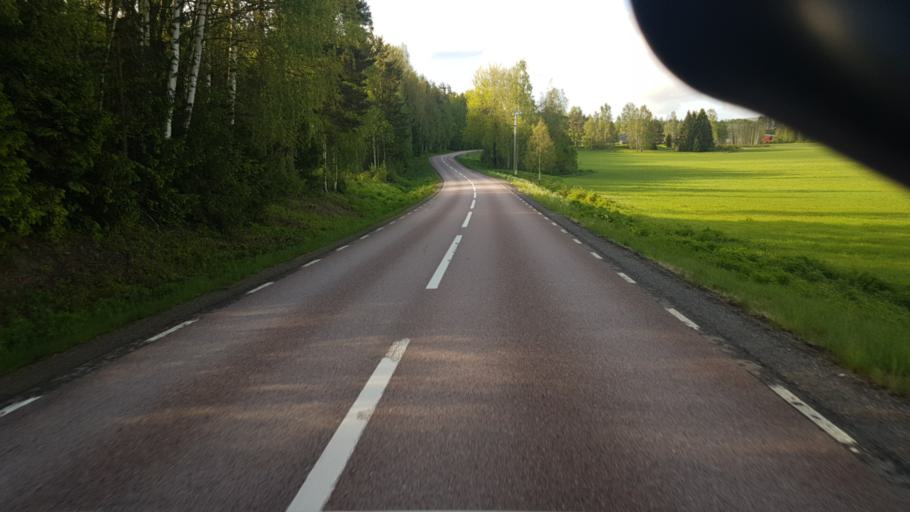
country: SE
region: Vaermland
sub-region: Eda Kommun
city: Amotfors
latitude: 59.7511
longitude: 12.2112
